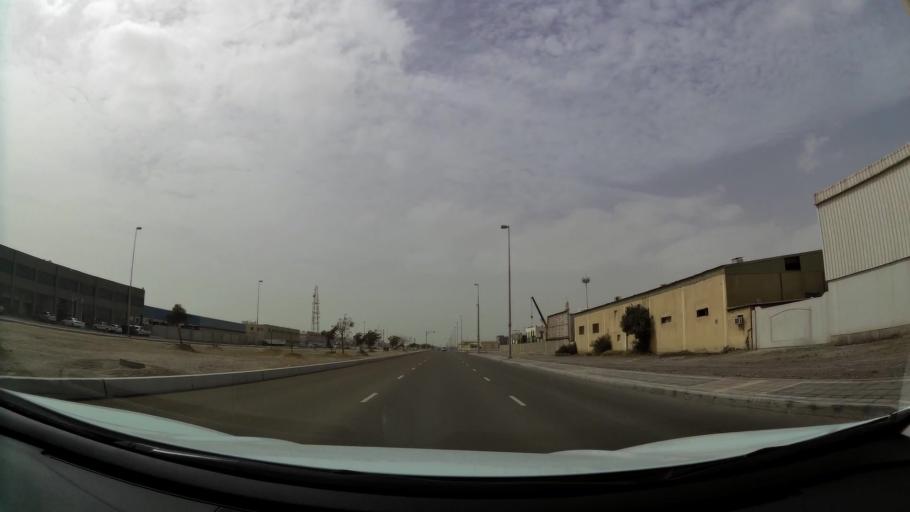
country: AE
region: Abu Dhabi
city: Abu Dhabi
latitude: 24.3680
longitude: 54.4884
